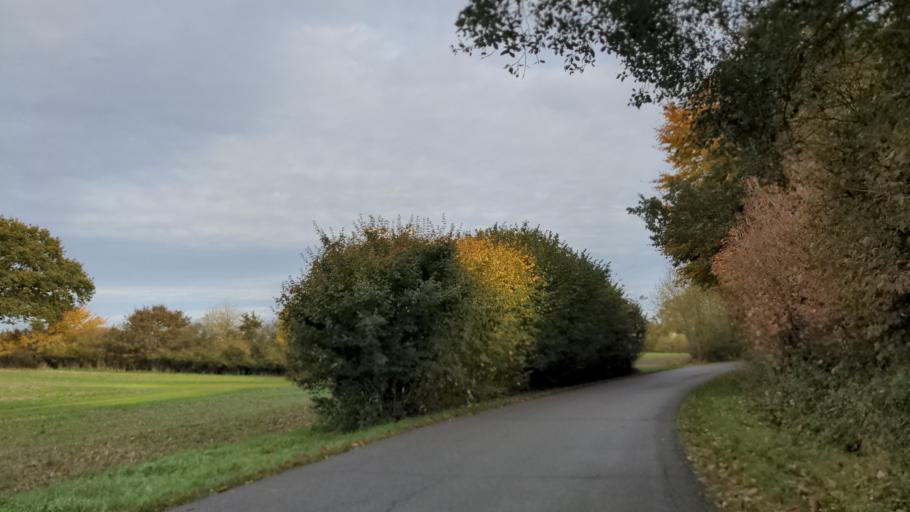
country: DE
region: Schleswig-Holstein
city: Bosdorf
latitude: 54.1145
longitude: 10.5258
